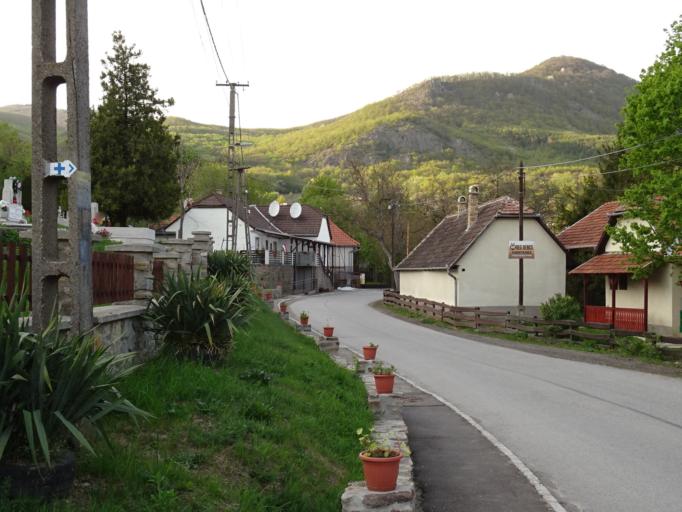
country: HU
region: Borsod-Abauj-Zemplen
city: Gonc
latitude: 48.5446
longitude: 21.4860
